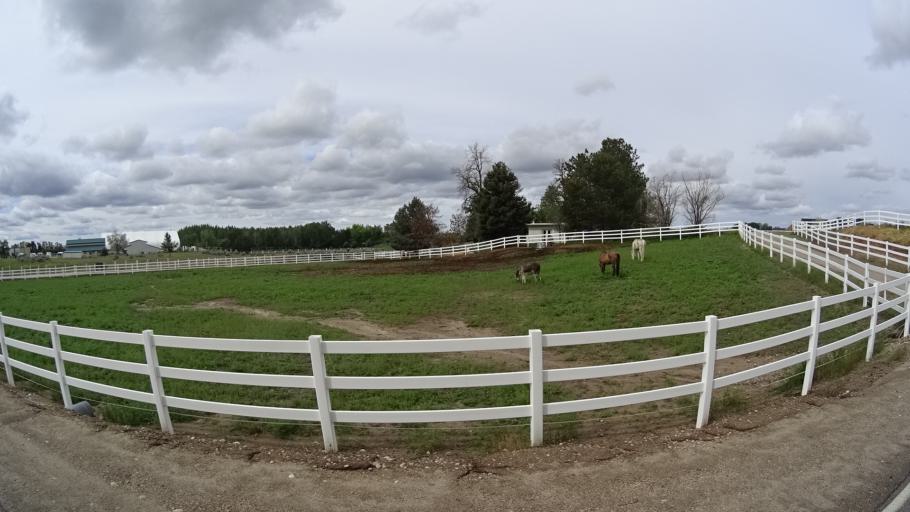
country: US
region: Idaho
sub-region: Ada County
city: Eagle
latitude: 43.7333
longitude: -116.3559
